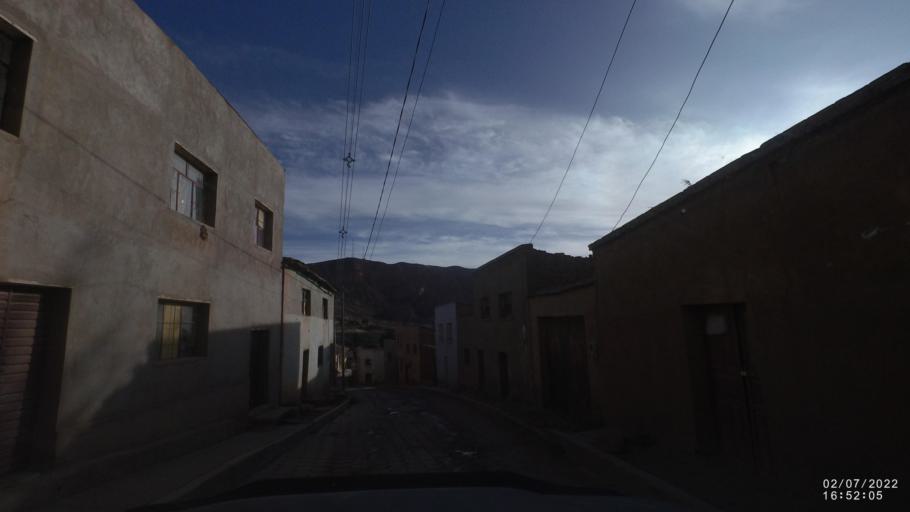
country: BO
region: Cochabamba
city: Irpa Irpa
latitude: -17.9692
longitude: -66.5358
